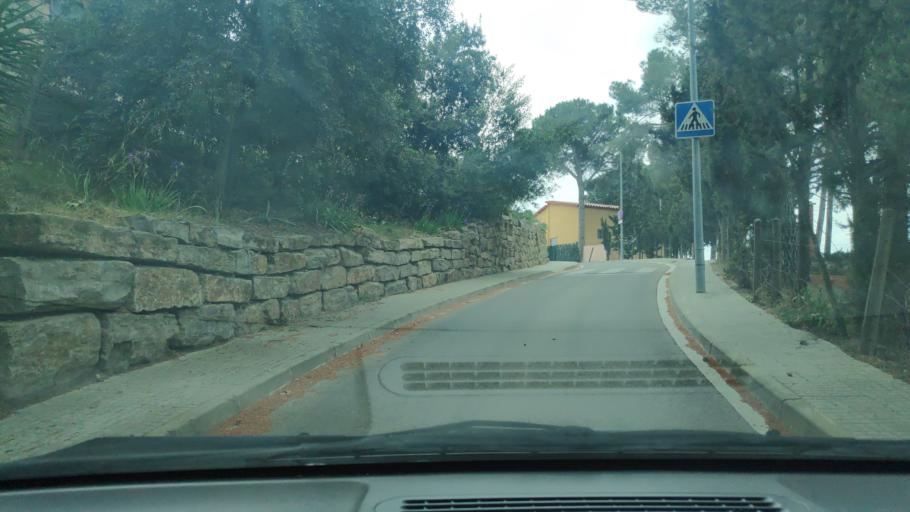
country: ES
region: Catalonia
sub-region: Provincia de Barcelona
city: Sant Quirze del Valles
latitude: 41.5107
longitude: 2.0603
